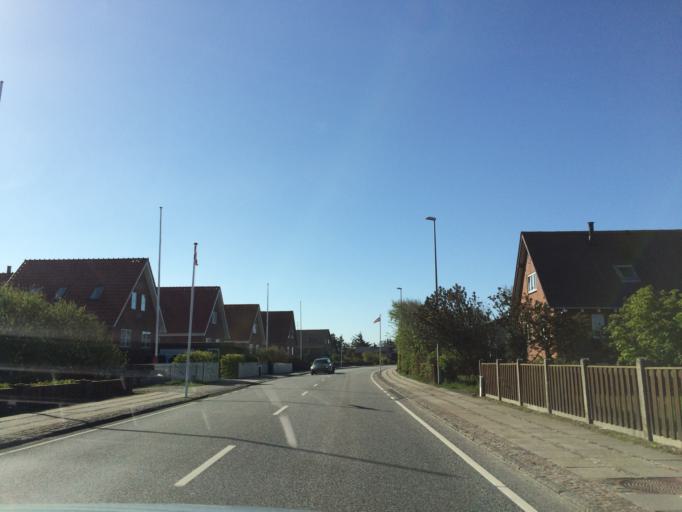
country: DK
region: Central Jutland
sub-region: Ringkobing-Skjern Kommune
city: Hvide Sande
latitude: 56.0138
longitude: 8.1287
